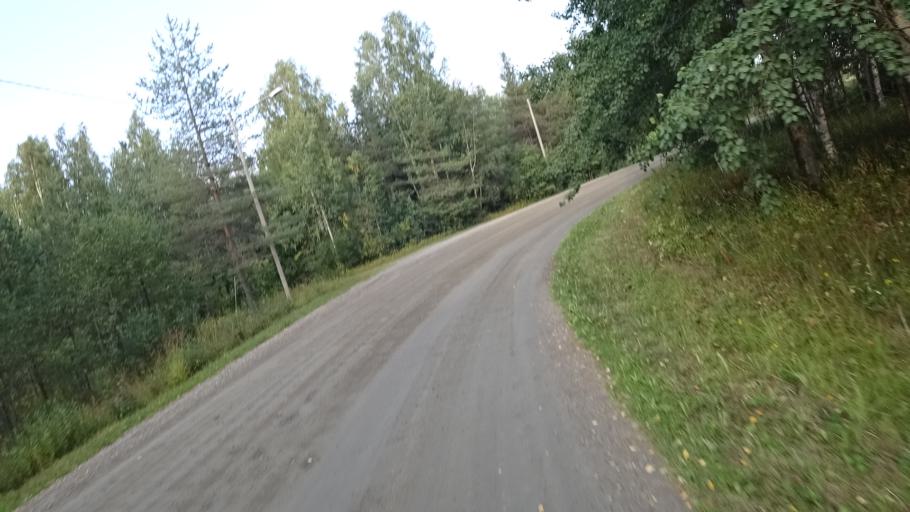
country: FI
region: North Karelia
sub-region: Joensuu
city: Ilomantsi
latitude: 62.6702
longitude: 30.9509
